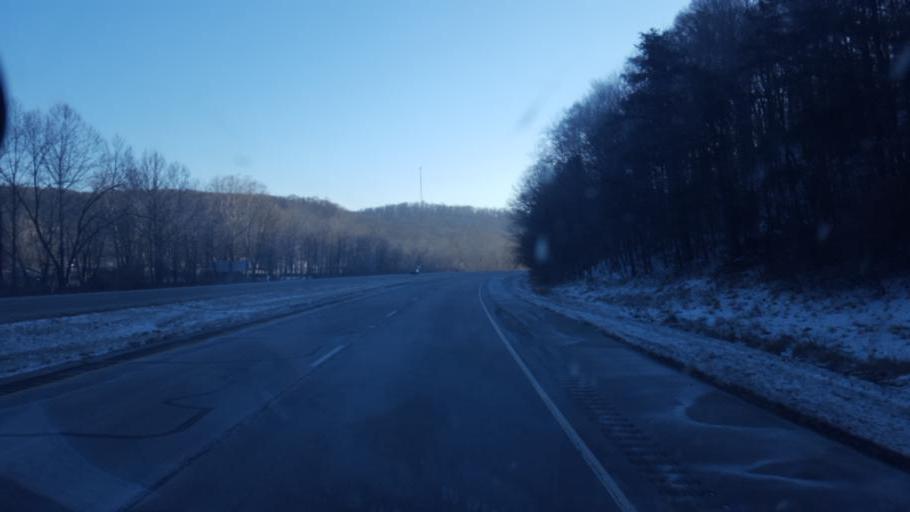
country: US
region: Ohio
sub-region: Pike County
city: Piketon
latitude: 39.0612
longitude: -83.0869
